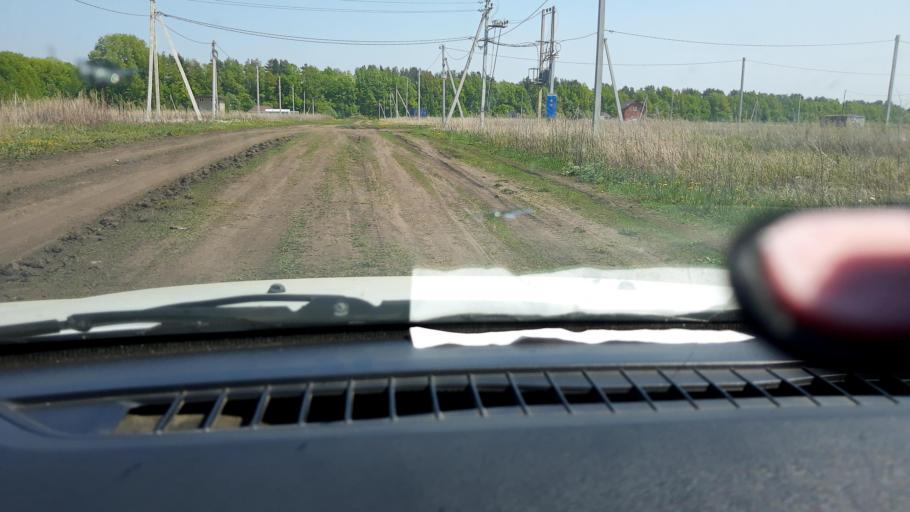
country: RU
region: Bashkortostan
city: Kabakovo
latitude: 54.6982
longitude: 56.1750
